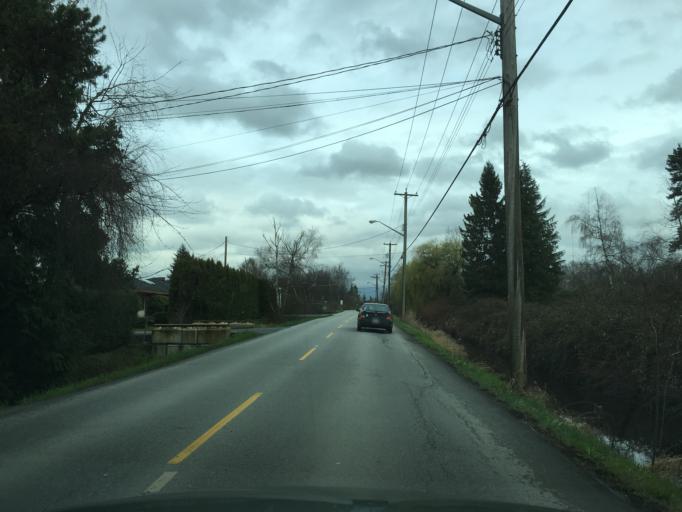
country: CA
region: British Columbia
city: Ladner
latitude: 49.1538
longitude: -123.0691
